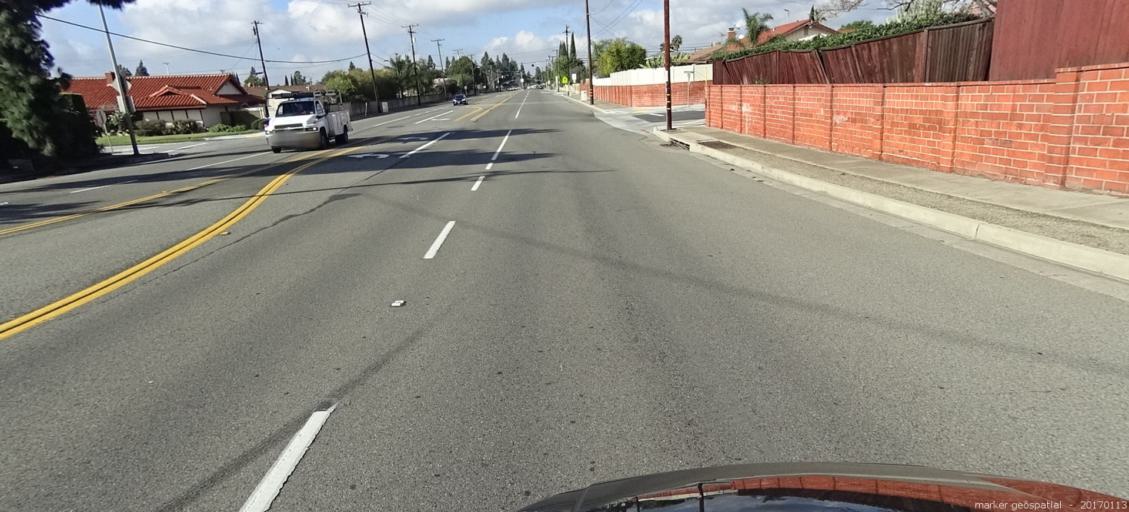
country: US
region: California
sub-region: Orange County
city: Placentia
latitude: 33.8894
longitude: -117.8490
